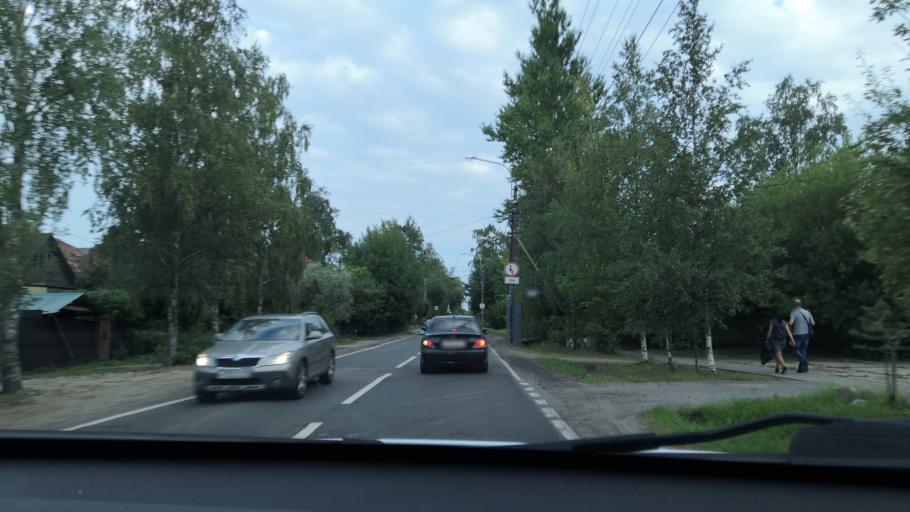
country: RU
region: St.-Petersburg
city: Pushkin
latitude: 59.7011
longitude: 30.4085
